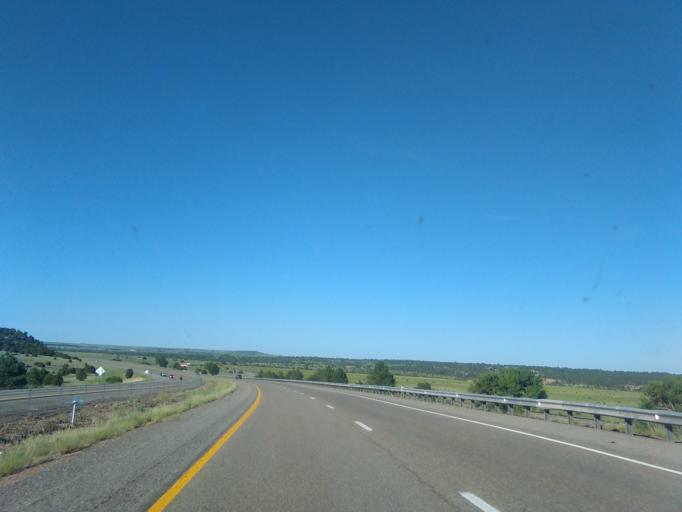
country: US
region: New Mexico
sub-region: San Miguel County
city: Las Vegas
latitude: 35.5265
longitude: -105.2367
